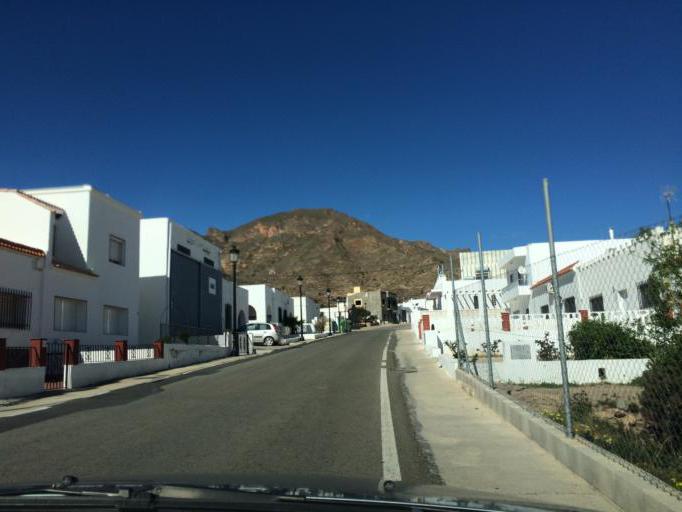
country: ES
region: Andalusia
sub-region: Provincia de Almeria
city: Nijar
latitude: 36.9594
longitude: -2.2070
